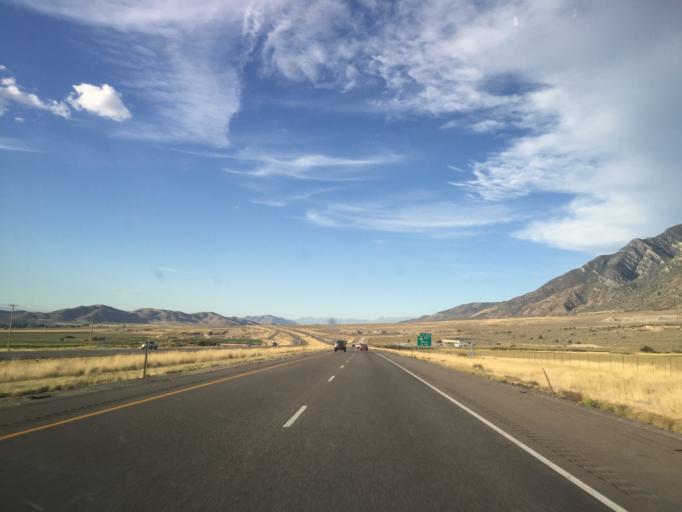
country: US
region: Utah
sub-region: Juab County
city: Mona
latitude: 39.8101
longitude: -111.8346
